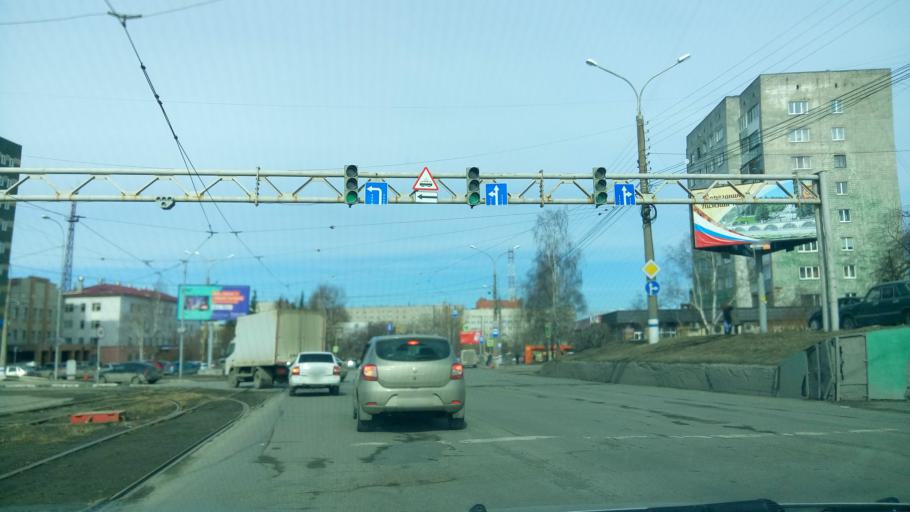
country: RU
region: Sverdlovsk
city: Nizhniy Tagil
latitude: 57.9084
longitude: 59.9475
